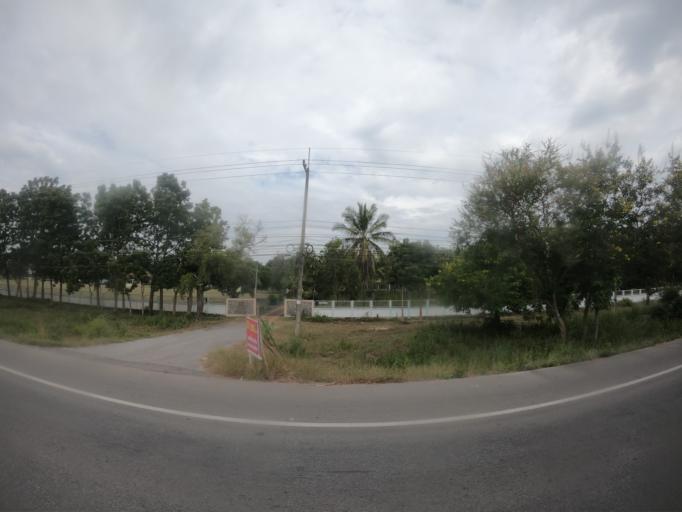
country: TH
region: Kalasin
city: Khong Chai
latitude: 16.1429
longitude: 103.4221
